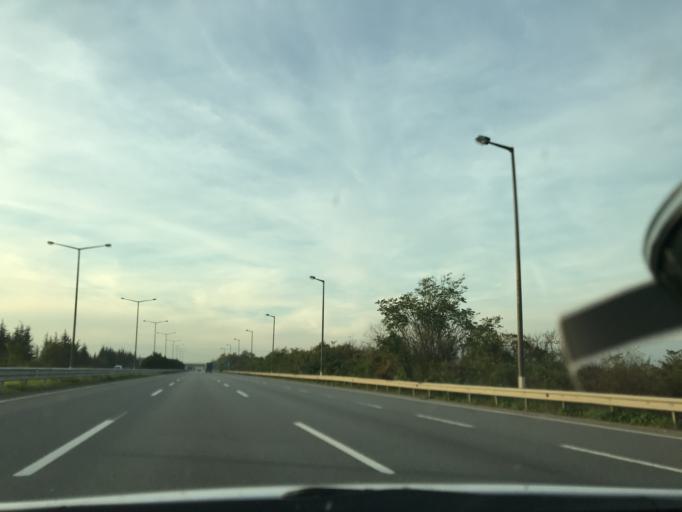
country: TR
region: Duzce
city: Cilimli
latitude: 40.8333
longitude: 31.0381
